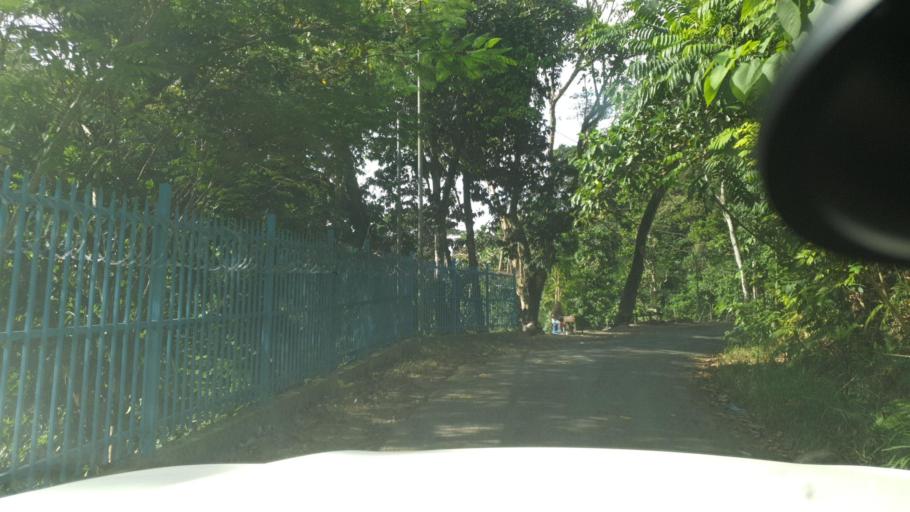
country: SB
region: Guadalcanal
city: Honiara
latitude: -9.4369
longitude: 159.9401
